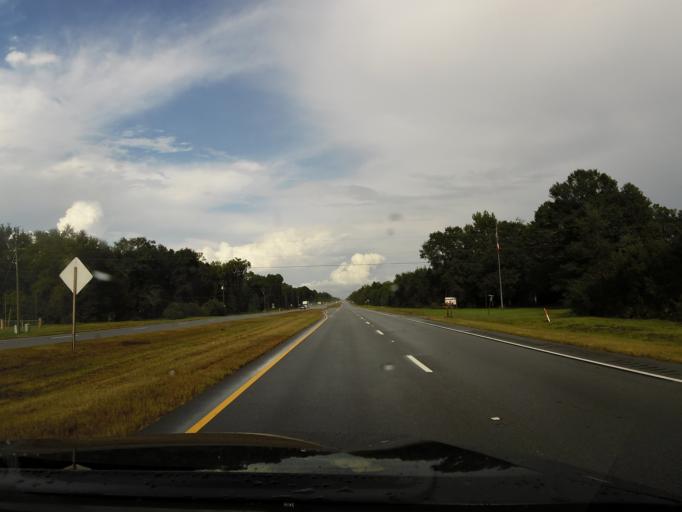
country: US
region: Georgia
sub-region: Long County
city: Ludowici
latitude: 31.7320
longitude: -81.7105
